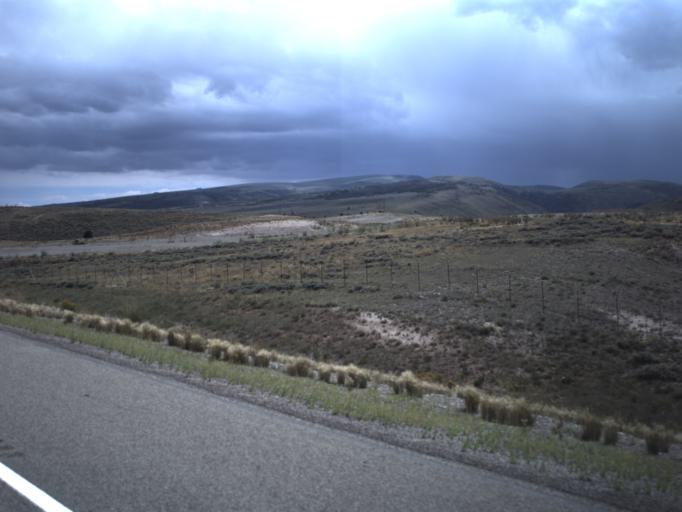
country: US
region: Utah
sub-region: Carbon County
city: Helper
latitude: 39.8484
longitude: -111.0074
